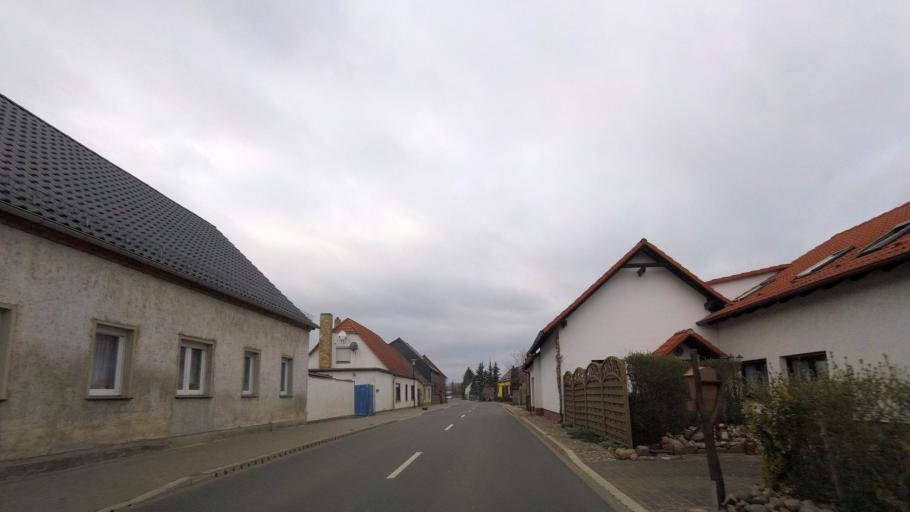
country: DE
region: Saxony-Anhalt
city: Kemberg
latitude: 51.7740
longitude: 12.6322
